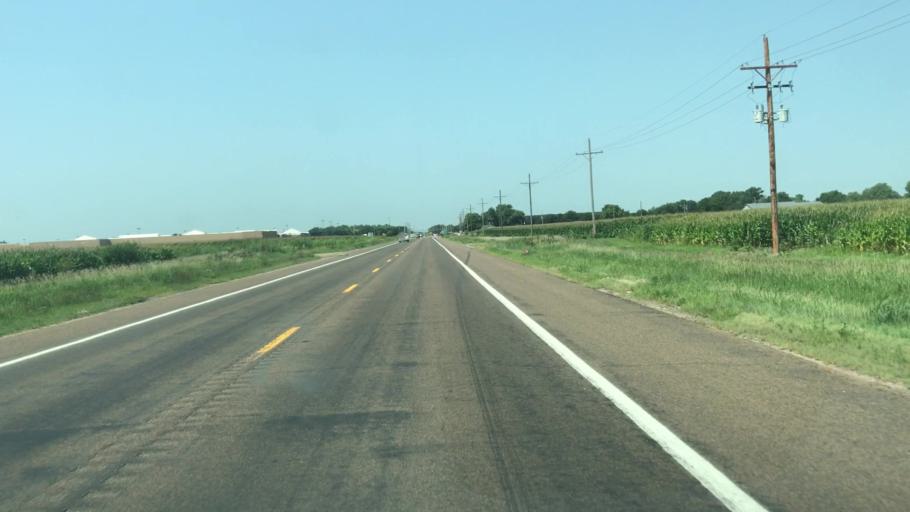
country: US
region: Nebraska
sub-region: Hall County
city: Grand Island
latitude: 40.8870
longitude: -98.3294
